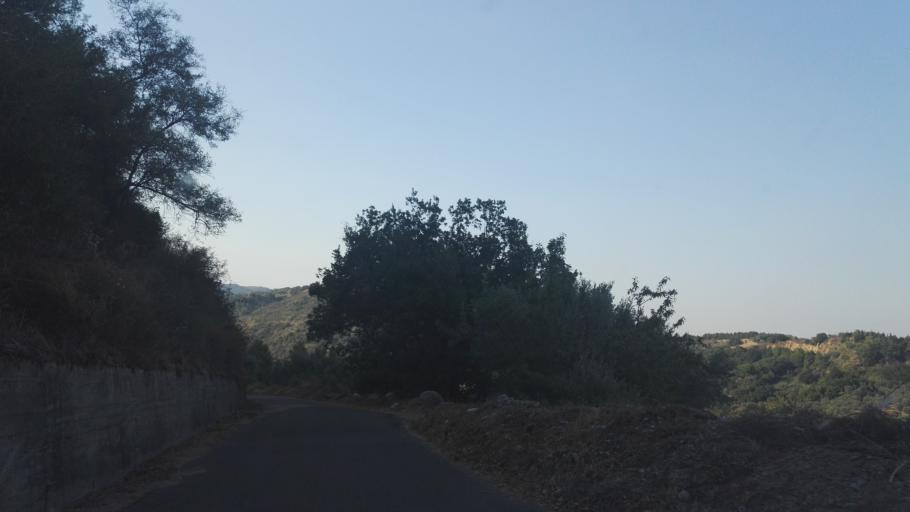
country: IT
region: Calabria
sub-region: Provincia di Reggio Calabria
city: Placanica
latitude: 38.4181
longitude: 16.4476
